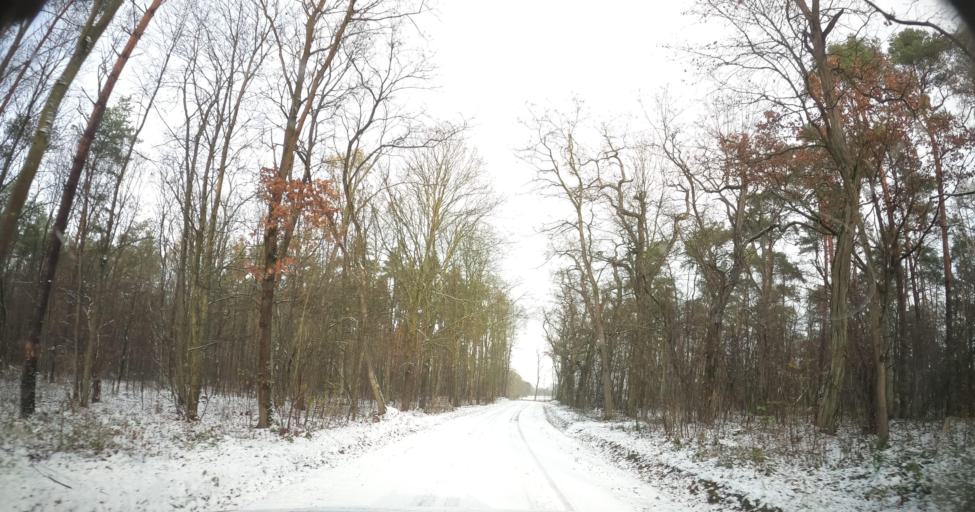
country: PL
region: West Pomeranian Voivodeship
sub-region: Powiat gryfinski
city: Mieszkowice
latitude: 52.7359
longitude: 14.4898
